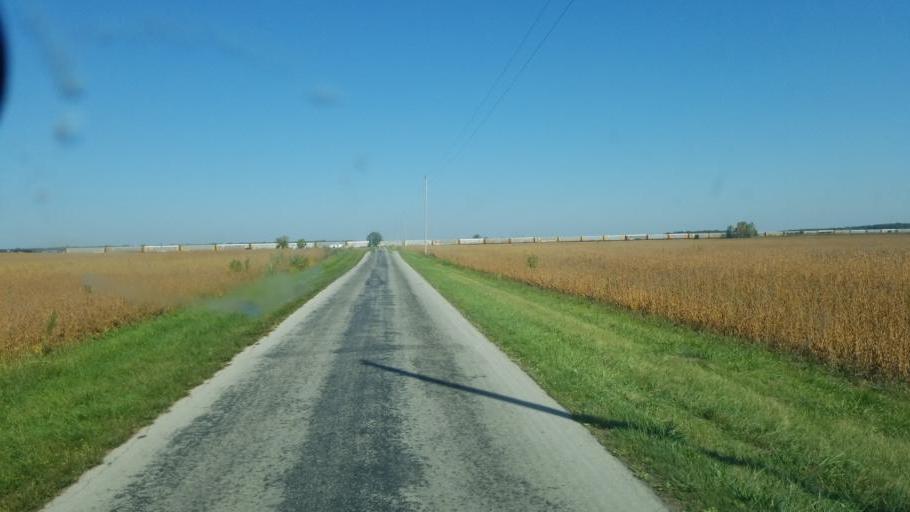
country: US
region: Ohio
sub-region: Hardin County
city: Kenton
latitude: 40.5392
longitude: -83.4832
